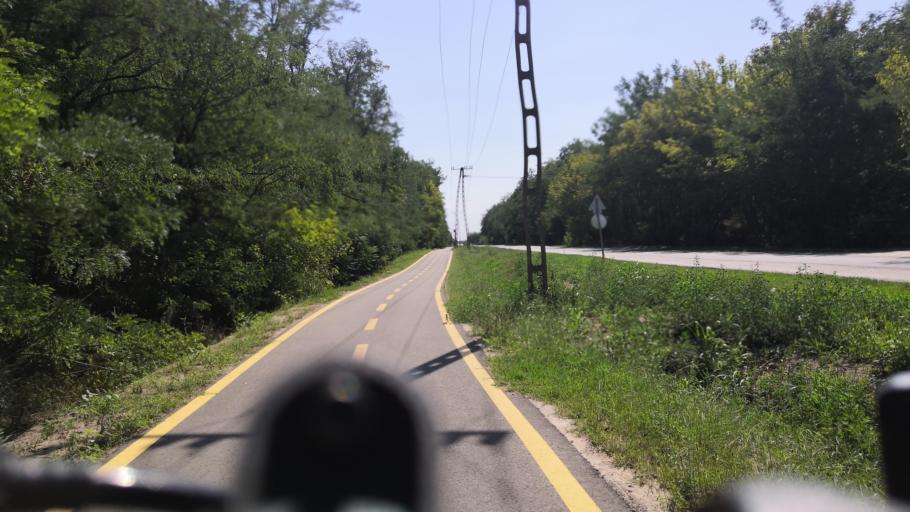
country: HU
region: Csongrad
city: Sandorfalva
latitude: 46.3826
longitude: 20.0880
